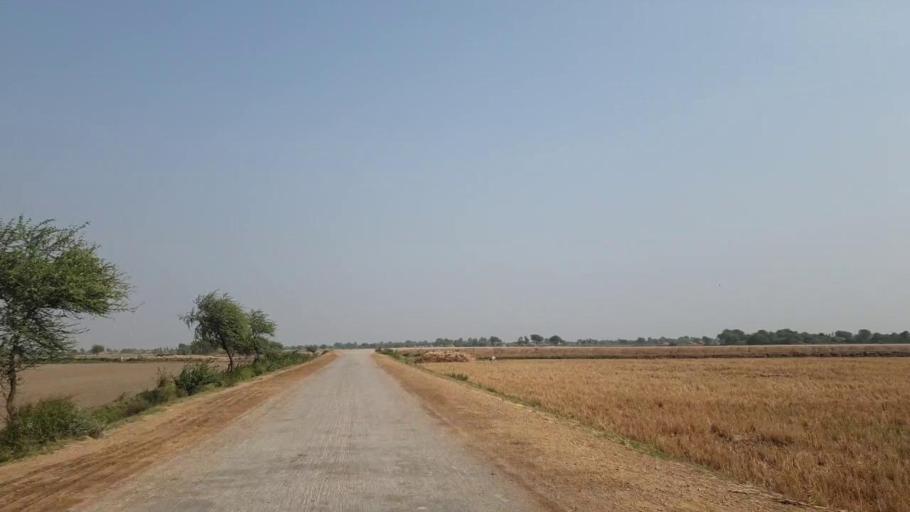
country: PK
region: Sindh
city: Matli
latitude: 24.9747
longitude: 68.5865
